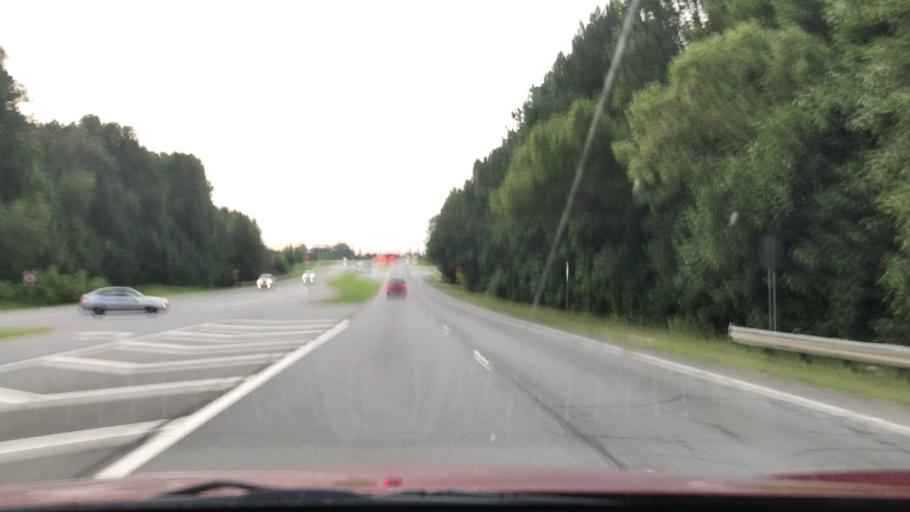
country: US
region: Georgia
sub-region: Gwinnett County
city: Lawrenceville
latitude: 34.0017
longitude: -83.9891
